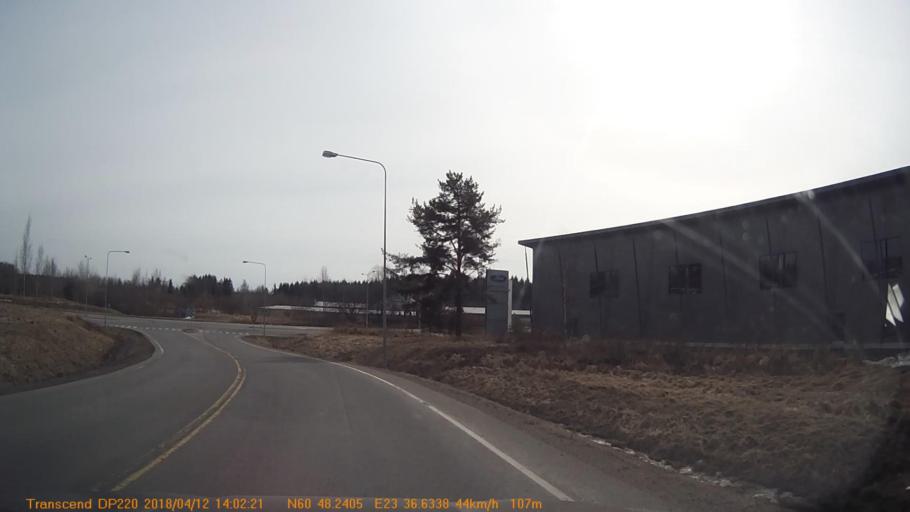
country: FI
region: Haeme
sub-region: Forssa
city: Forssa
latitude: 60.8040
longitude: 23.6107
